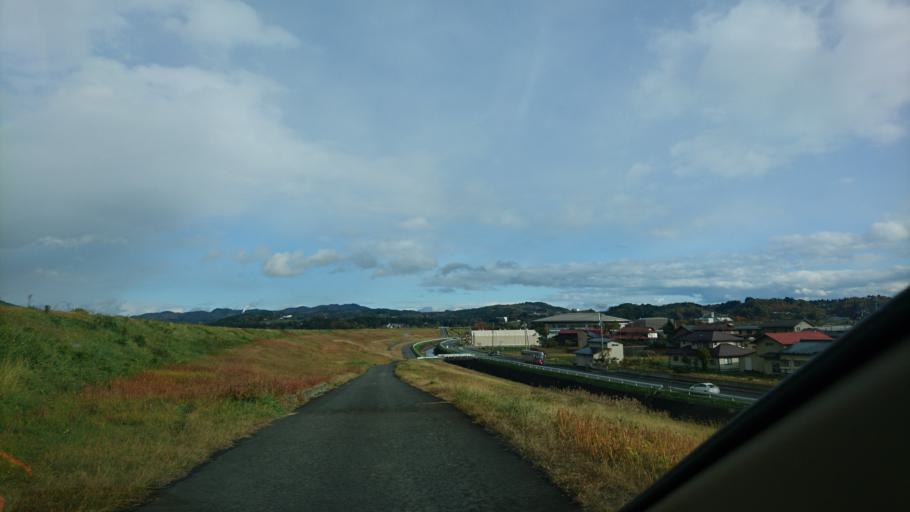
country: JP
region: Iwate
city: Ichinoseki
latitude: 38.9433
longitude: 141.1496
